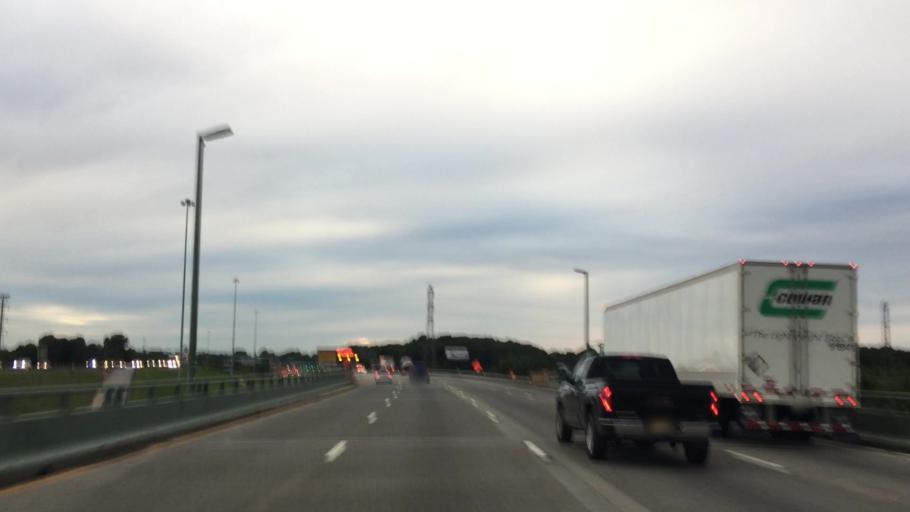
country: US
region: Delaware
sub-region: New Castle County
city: New Castle
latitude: 39.6949
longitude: -75.5360
